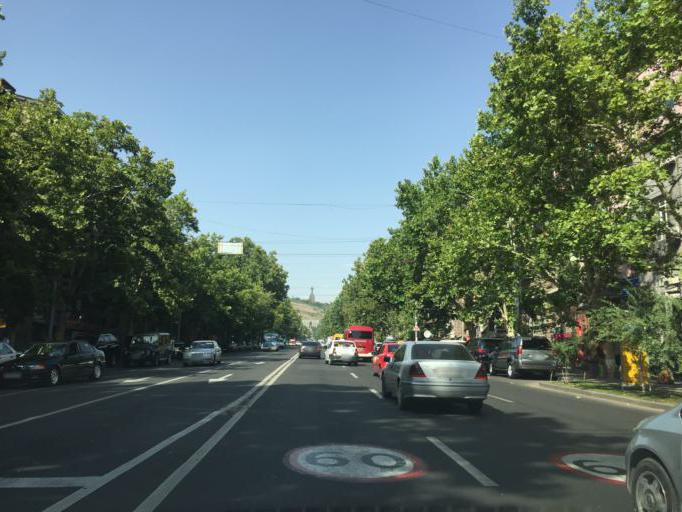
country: AM
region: Yerevan
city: Yerevan
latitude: 40.1838
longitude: 44.5111
